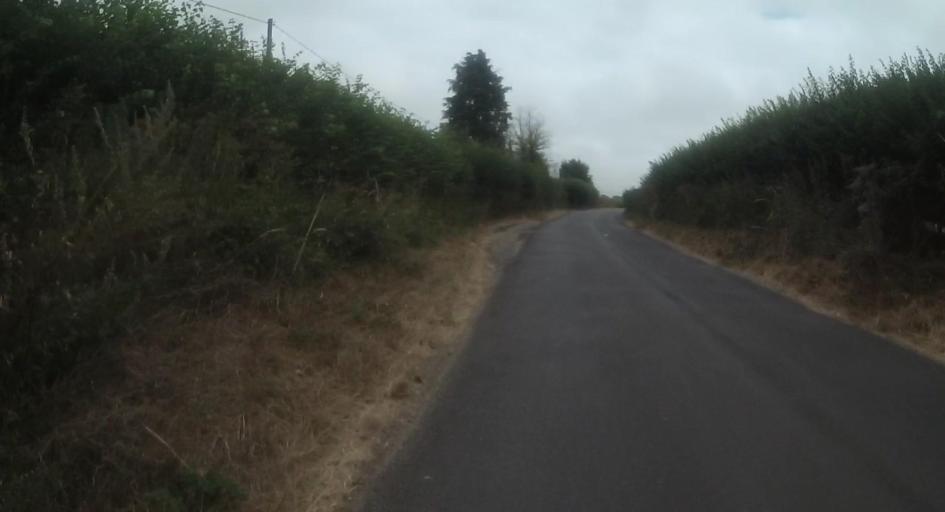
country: GB
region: England
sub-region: Dorset
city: Bovington Camp
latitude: 50.7108
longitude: -2.2930
